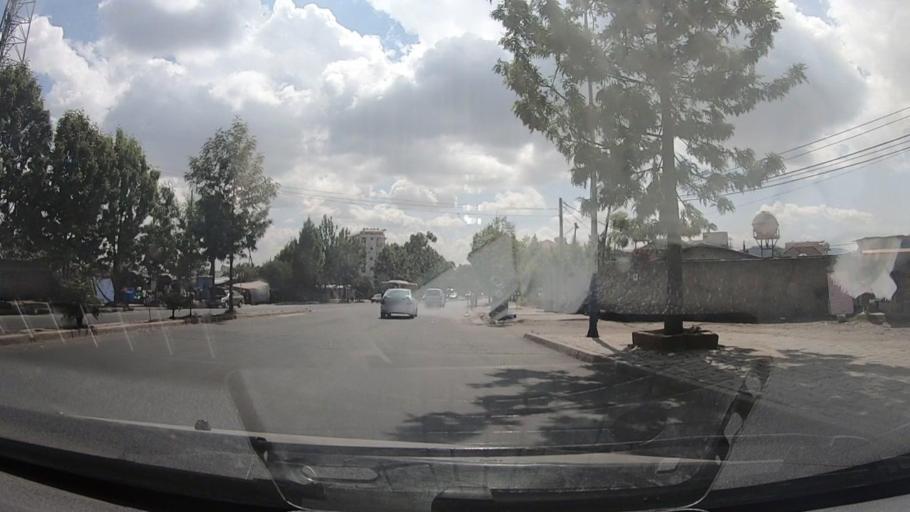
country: ET
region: Adis Abeba
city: Addis Ababa
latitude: 8.9742
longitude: 38.7243
